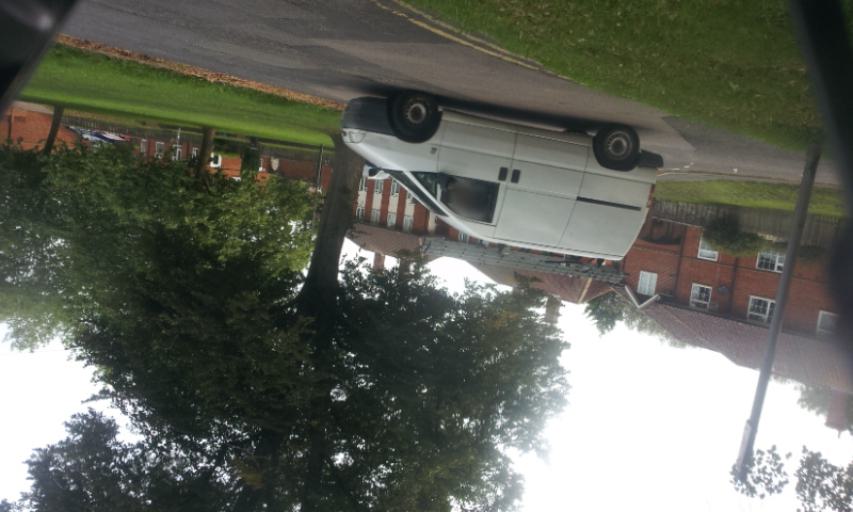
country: GB
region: England
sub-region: Kent
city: Tonbridge
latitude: 51.1854
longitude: 0.2842
